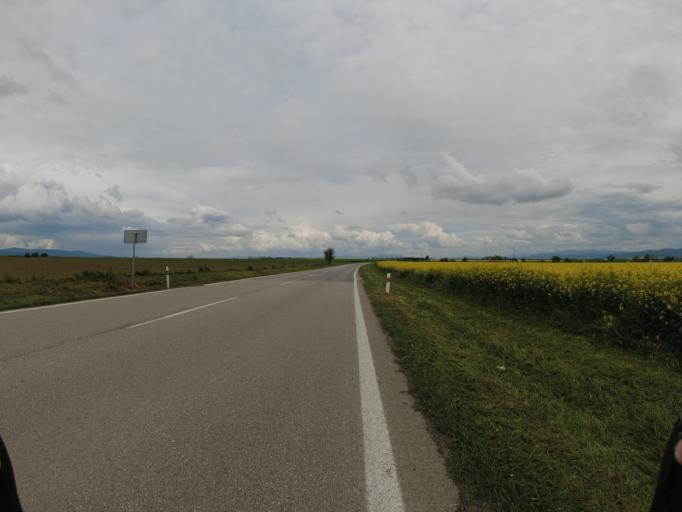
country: SK
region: Nitriansky
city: Banovce nad Bebravou
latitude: 48.5436
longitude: 18.1047
